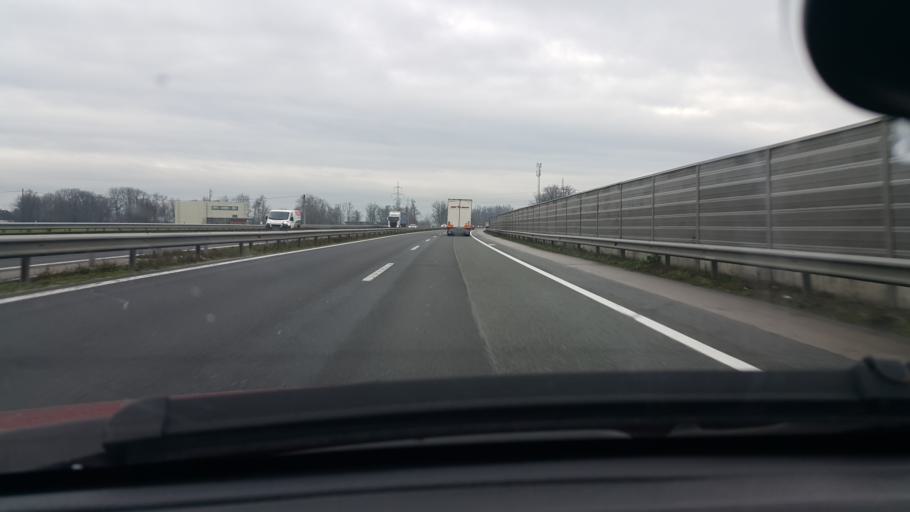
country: SI
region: Dol pri Ljubljani
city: Dol pri Ljubljani
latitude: 46.1079
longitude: 14.5993
